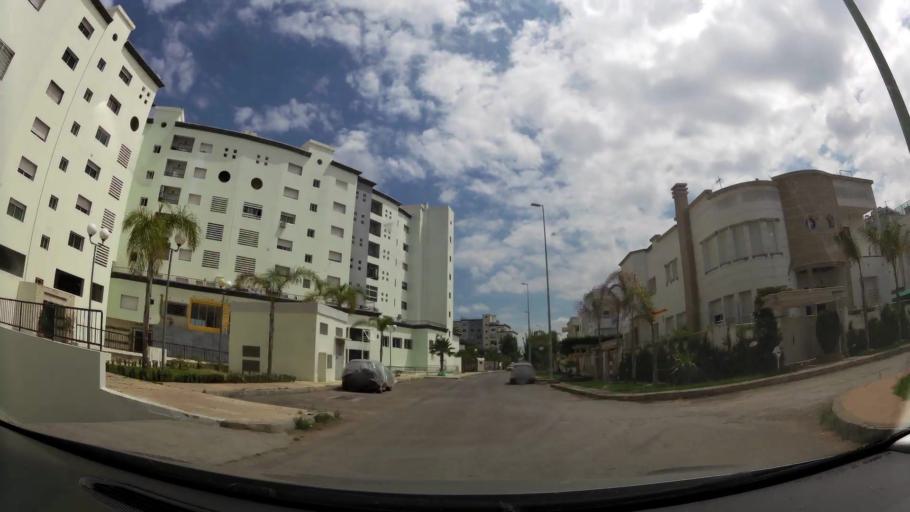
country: MA
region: Gharb-Chrarda-Beni Hssen
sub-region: Kenitra Province
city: Kenitra
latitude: 34.2503
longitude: -6.6028
